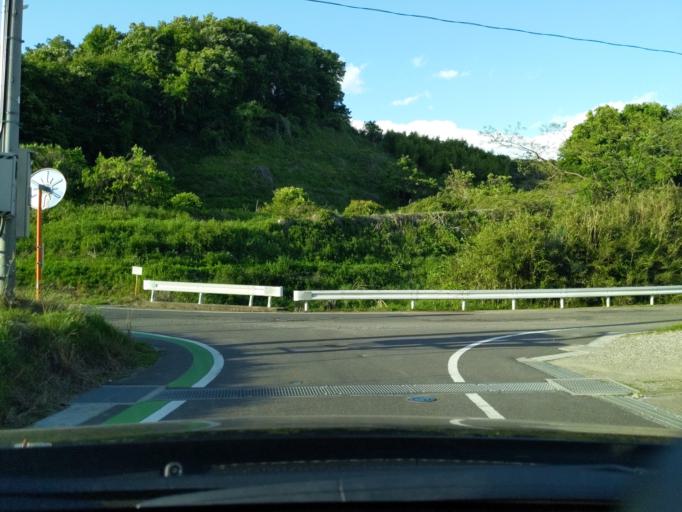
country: JP
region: Fukushima
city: Miharu
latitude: 37.4301
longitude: 140.4351
